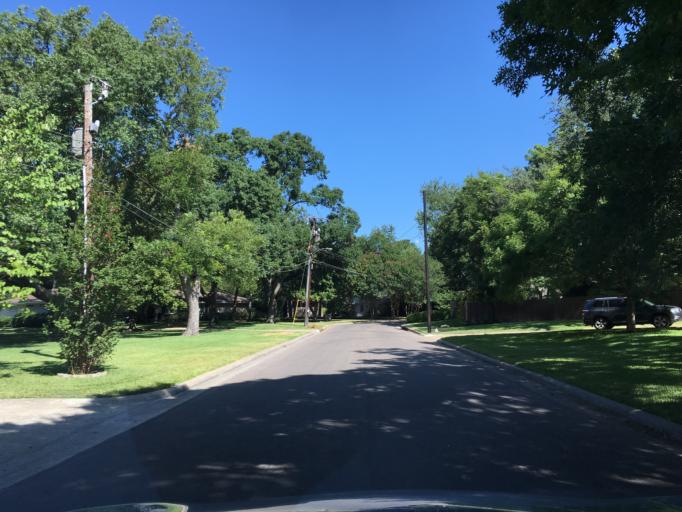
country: US
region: Texas
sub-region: Dallas County
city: Garland
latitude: 32.8677
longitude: -96.6982
